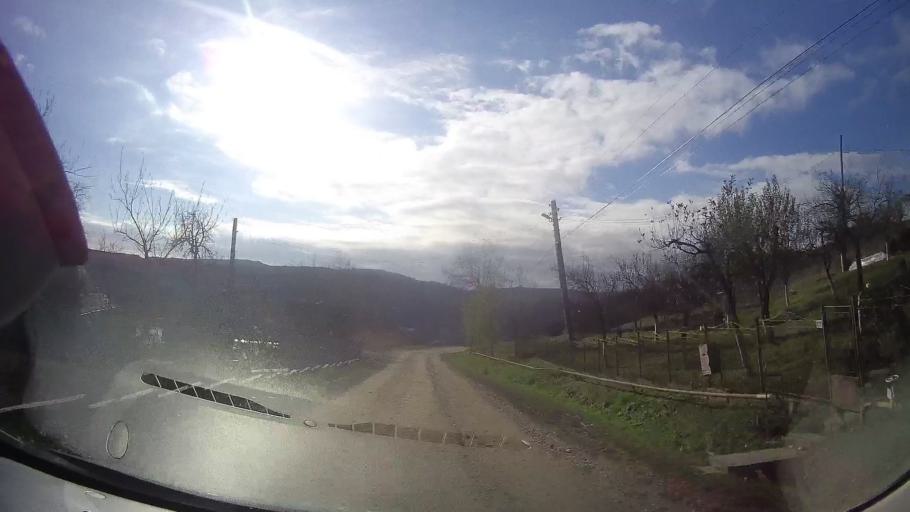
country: RO
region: Mures
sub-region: Comuna Papiu Ilarian
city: Papiu Ilarian
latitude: 46.5643
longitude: 24.2097
